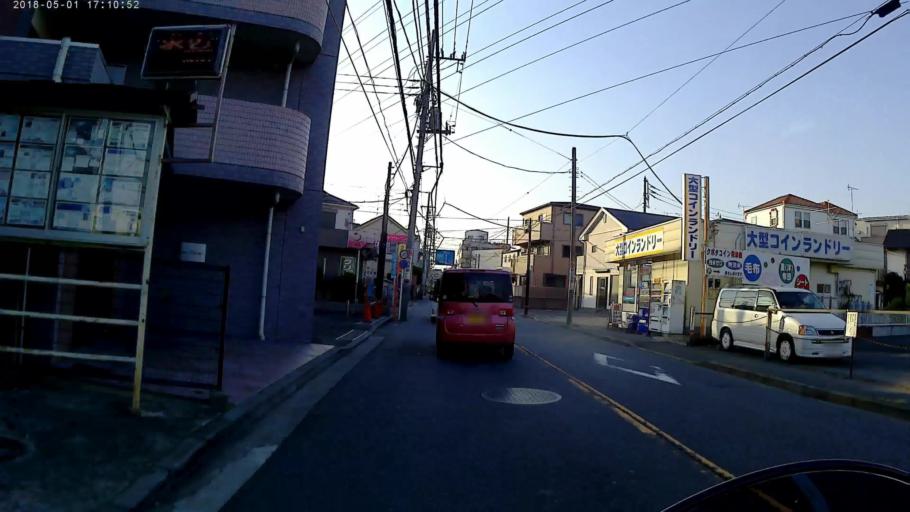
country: JP
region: Kanagawa
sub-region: Kawasaki-shi
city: Kawasaki
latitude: 35.5477
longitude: 139.6232
